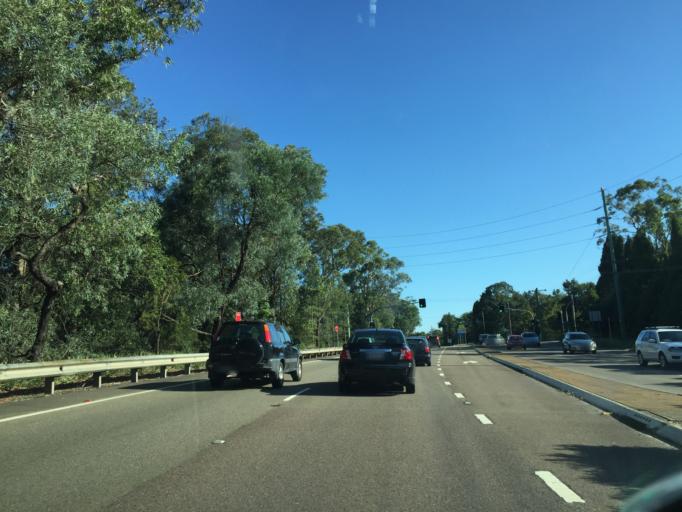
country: AU
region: New South Wales
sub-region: Blue Mountains Municipality
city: Blaxland
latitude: -33.7354
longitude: 150.6053
